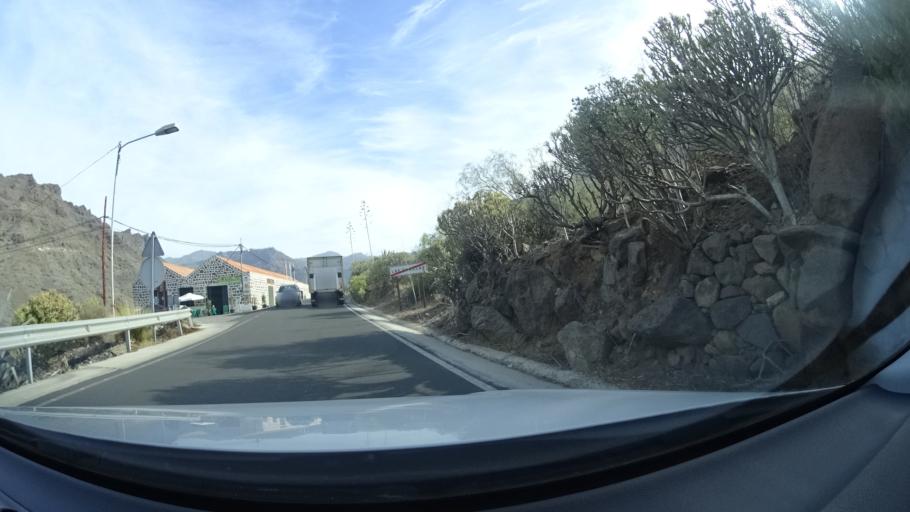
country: ES
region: Canary Islands
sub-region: Provincia de Las Palmas
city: Mogan
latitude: 27.8722
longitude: -15.7319
